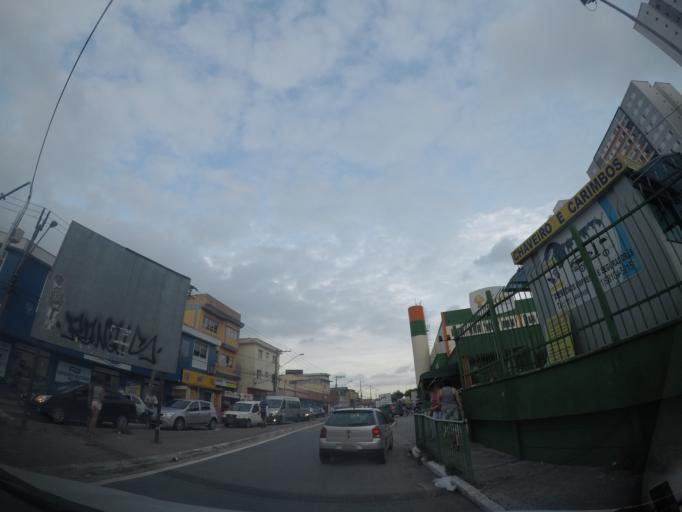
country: BR
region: Sao Paulo
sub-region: Guarulhos
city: Guarulhos
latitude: -23.4530
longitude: -46.5087
